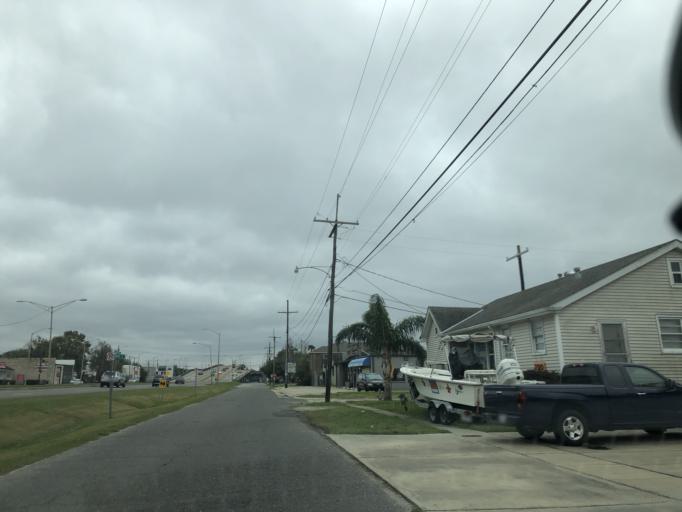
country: US
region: Louisiana
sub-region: Jefferson Parish
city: Metairie
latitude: 29.9800
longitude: -90.1564
